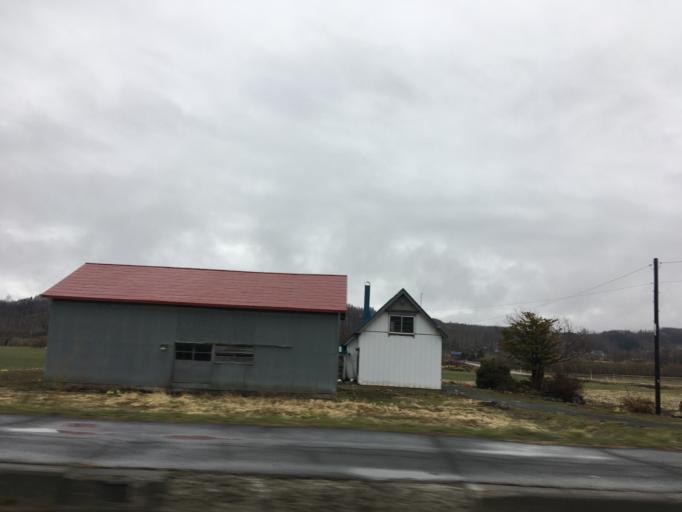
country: JP
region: Hokkaido
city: Nayoro
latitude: 44.1023
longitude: 142.4762
